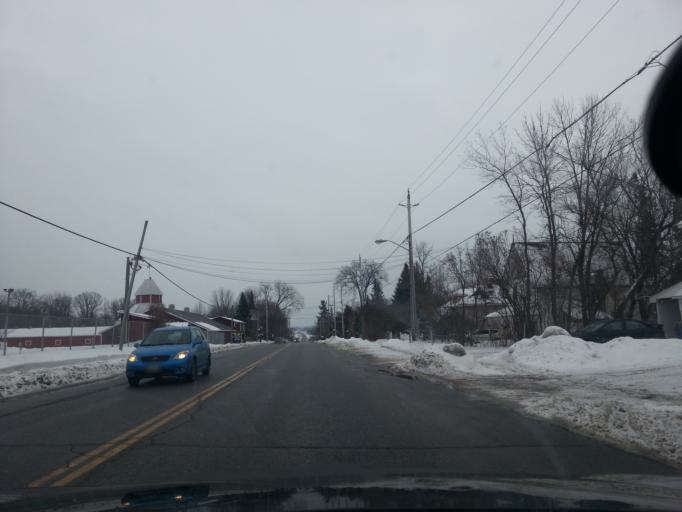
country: CA
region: Ontario
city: Bells Corners
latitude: 45.3474
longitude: -76.0394
